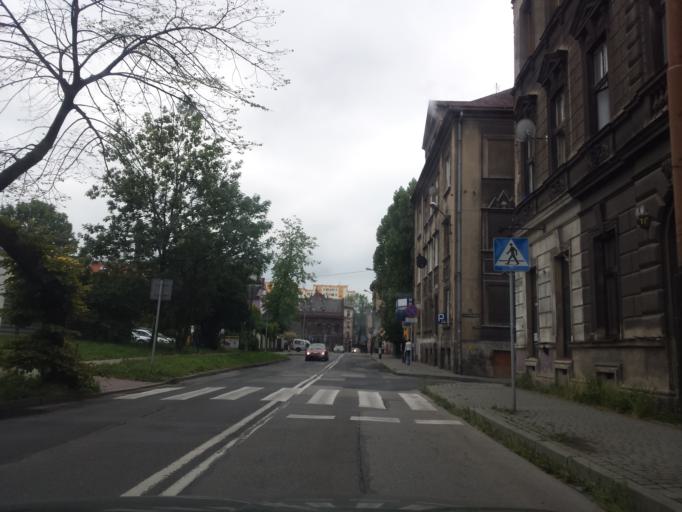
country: PL
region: Silesian Voivodeship
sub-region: Bielsko-Biala
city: Bielsko-Biala
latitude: 49.8239
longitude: 19.0566
